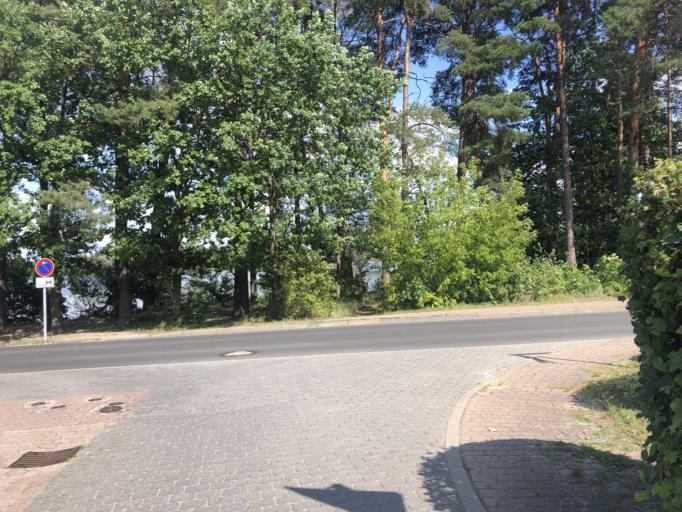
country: DE
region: Brandenburg
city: Mullrose
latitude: 52.2355
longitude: 14.4128
